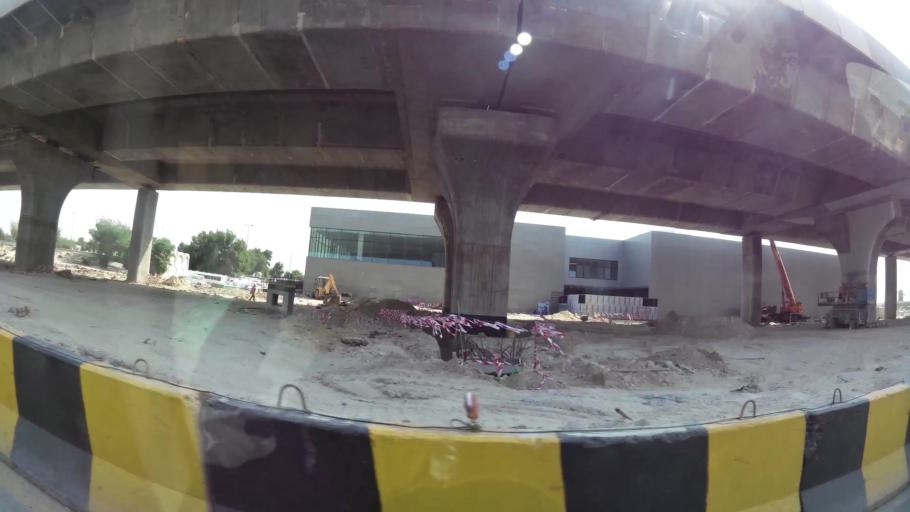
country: KW
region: Al Asimah
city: Ash Shamiyah
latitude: 29.3337
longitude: 47.9335
